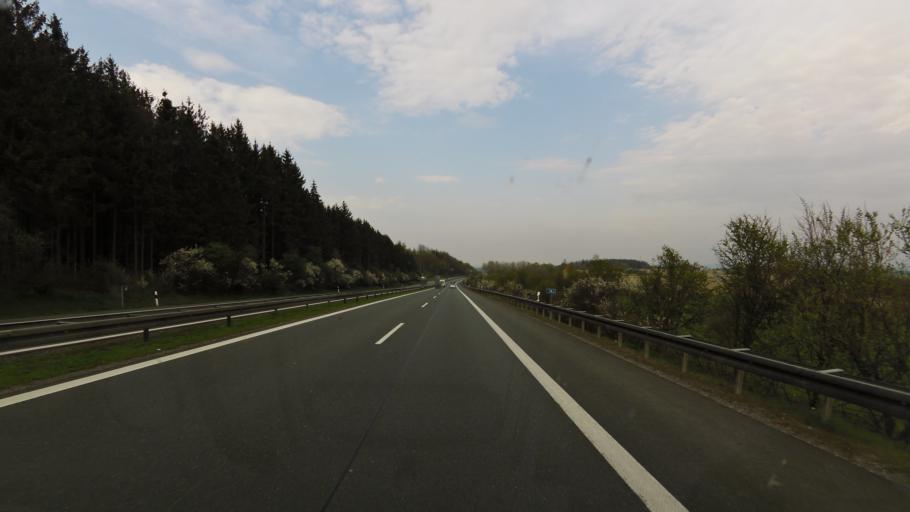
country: DE
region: Bavaria
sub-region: Upper Franconia
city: Trogen
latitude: 50.4001
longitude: 12.0138
